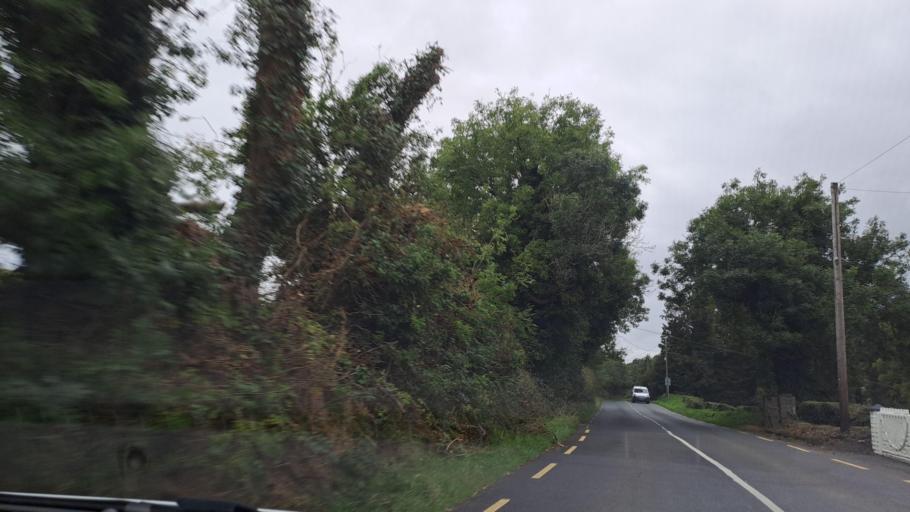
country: IE
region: Ulster
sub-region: County Monaghan
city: Monaghan
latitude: 54.1196
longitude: -6.8943
